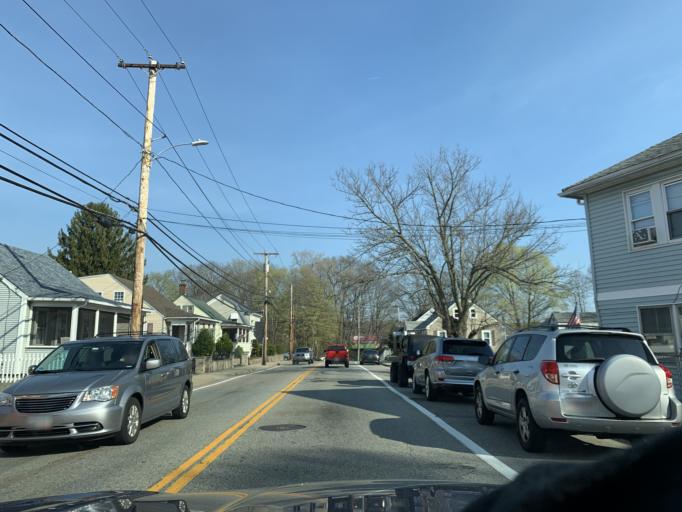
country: US
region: Rhode Island
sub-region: Kent County
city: West Warwick
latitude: 41.7193
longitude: -71.5250
